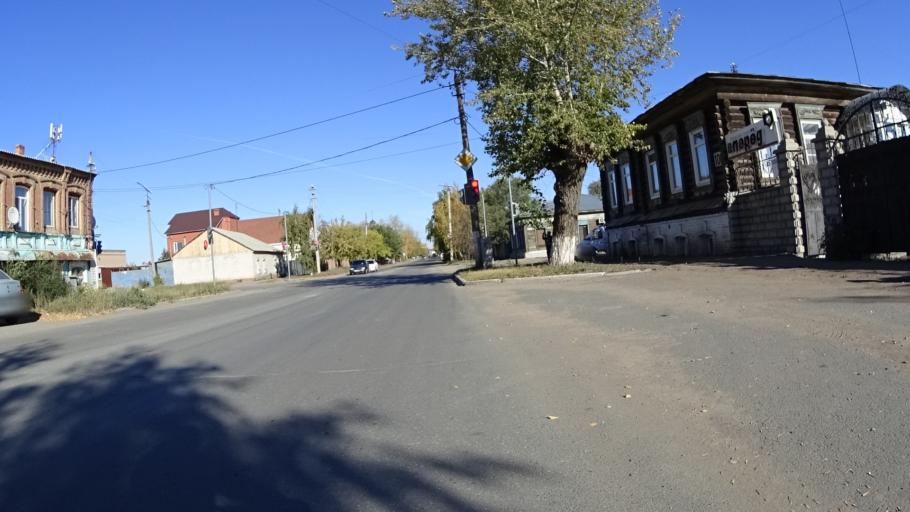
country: RU
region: Chelyabinsk
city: Troitsk
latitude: 54.0852
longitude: 61.5663
